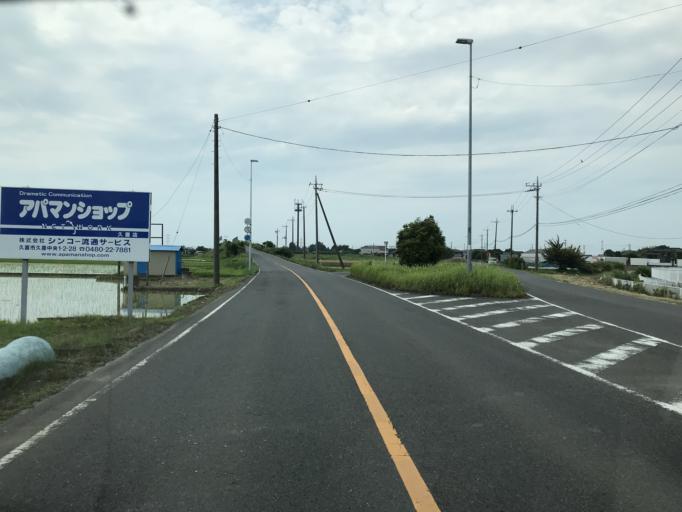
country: JP
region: Saitama
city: Kukichuo
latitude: 36.0832
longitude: 139.6424
